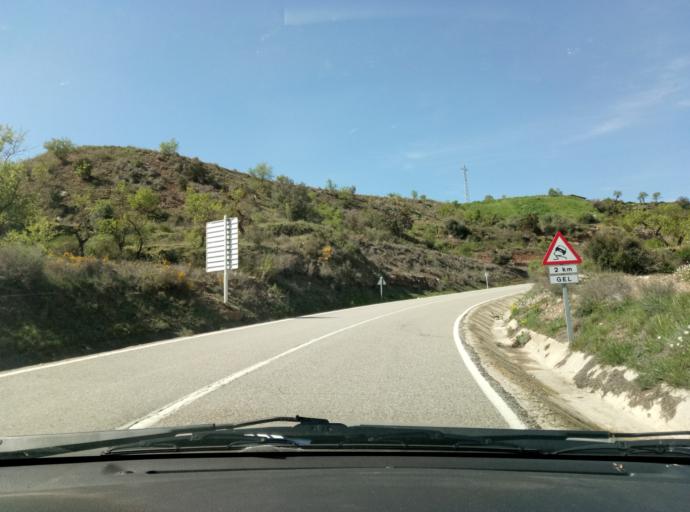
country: ES
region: Catalonia
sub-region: Provincia de Lleida
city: Vallbona de les Monges
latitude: 41.5495
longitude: 1.0314
